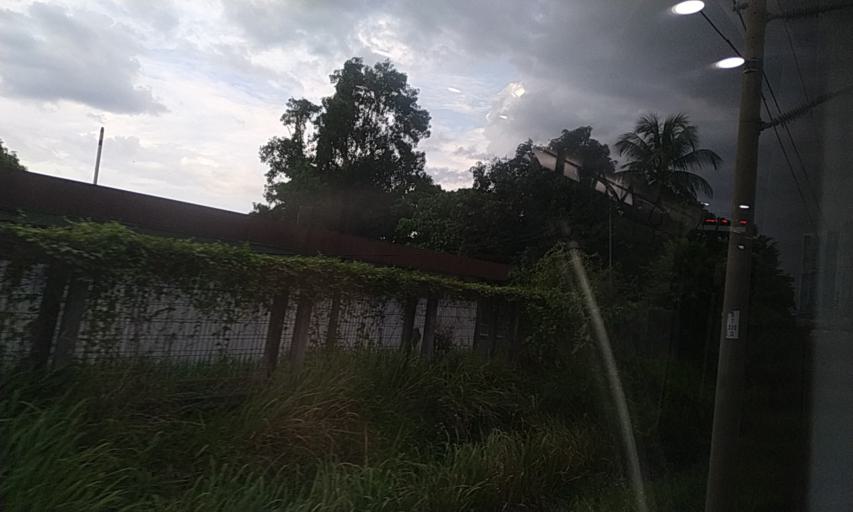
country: MY
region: Kuala Lumpur
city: Kuala Lumpur
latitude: 3.2286
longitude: 101.6730
